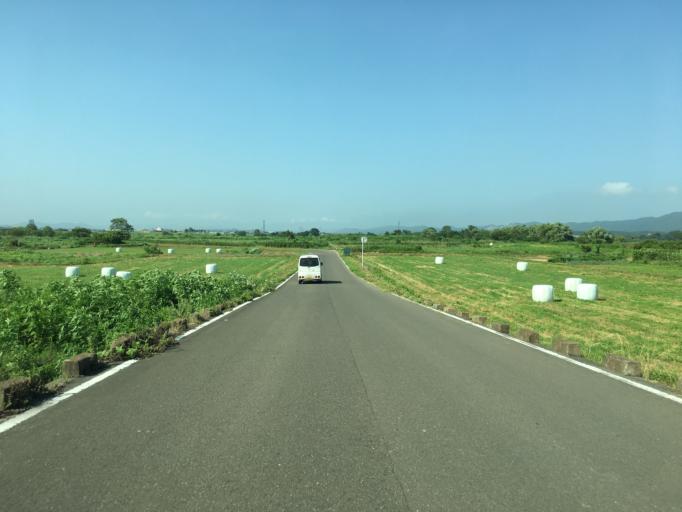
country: JP
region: Miyagi
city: Kakuda
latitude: 37.9608
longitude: 140.7898
